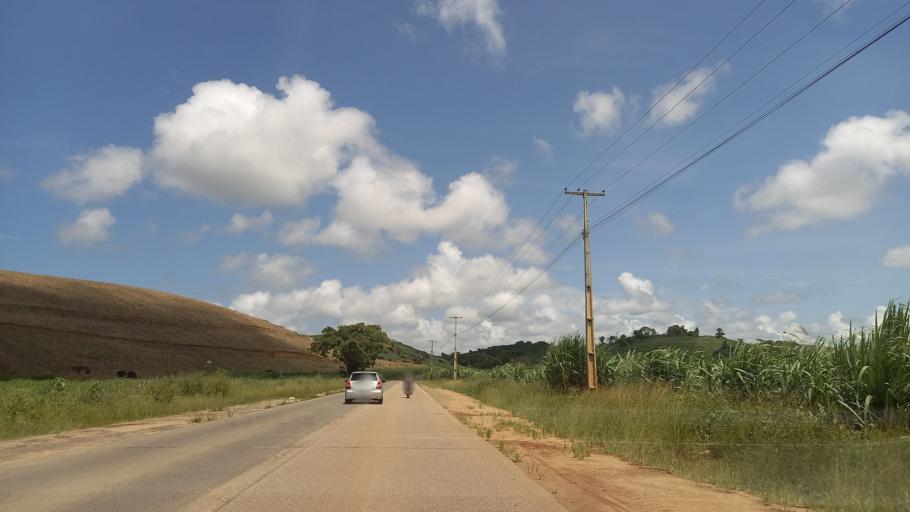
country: BR
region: Pernambuco
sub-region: Sirinhaem
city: Sirinhaem
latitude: -8.6065
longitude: -35.1170
